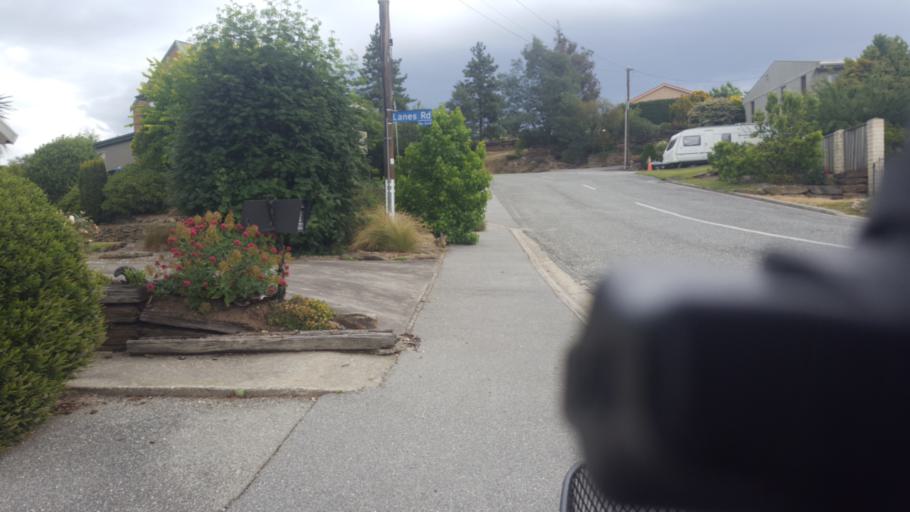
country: NZ
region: Otago
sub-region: Queenstown-Lakes District
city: Wanaka
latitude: -45.2631
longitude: 169.3777
